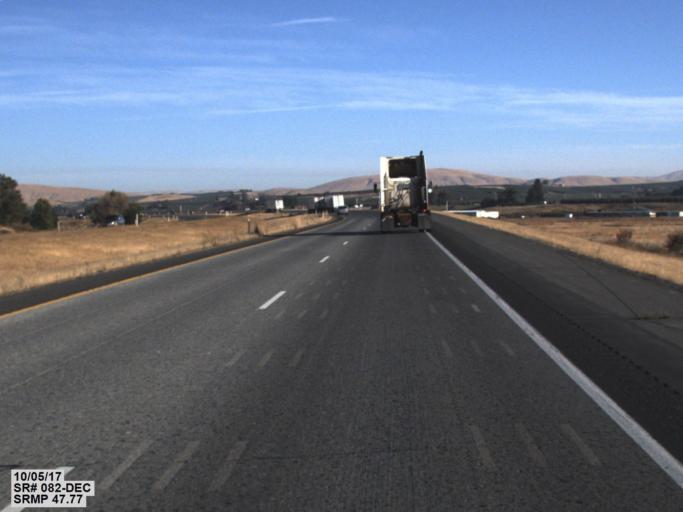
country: US
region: Washington
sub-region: Yakima County
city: Toppenish
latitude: 46.4383
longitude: -120.3451
